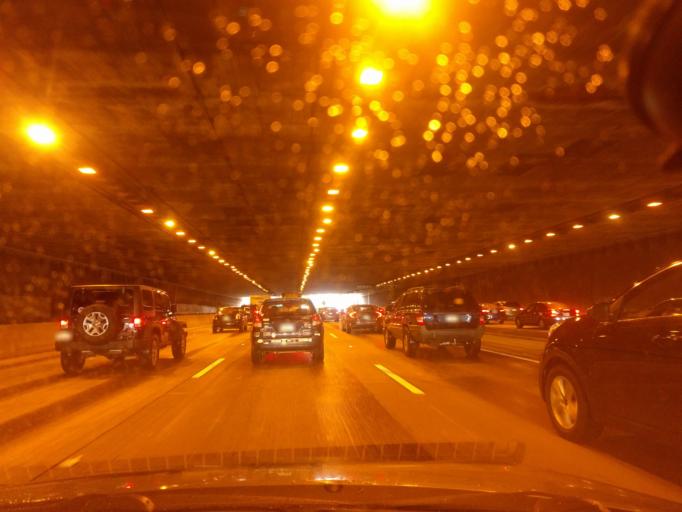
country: US
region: California
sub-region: San Diego County
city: San Diego
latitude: 32.7519
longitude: -117.1086
